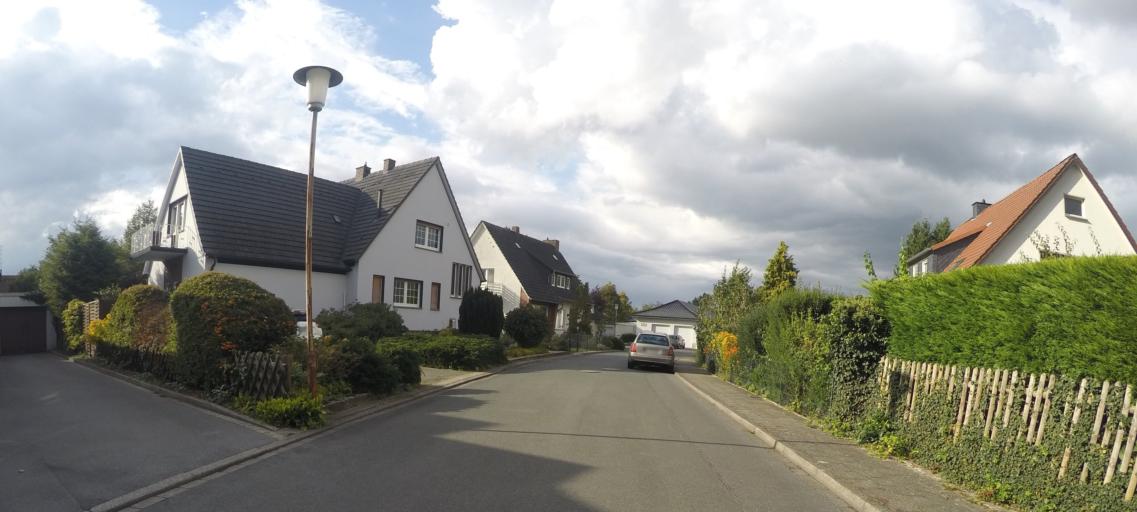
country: DE
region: North Rhine-Westphalia
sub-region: Regierungsbezirk Arnsberg
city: Lippstadt
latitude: 51.6864
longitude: 8.3533
